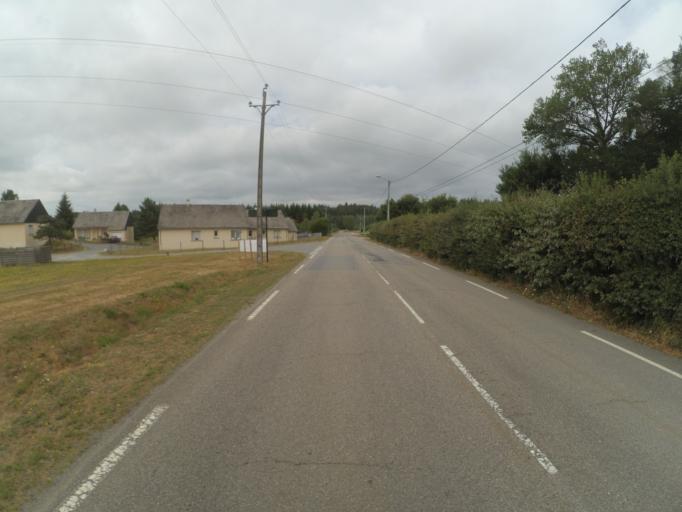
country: FR
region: Limousin
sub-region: Departement de la Correze
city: Meymac
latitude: 45.5031
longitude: 2.2226
